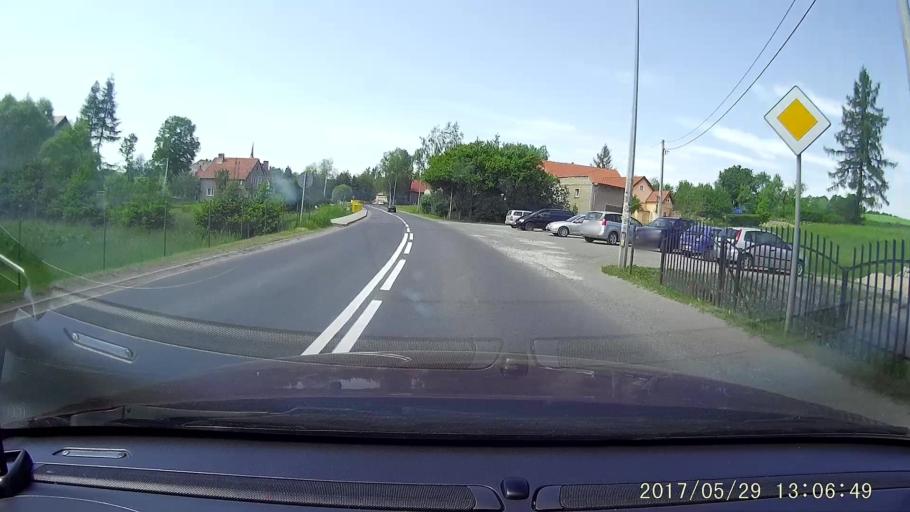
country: PL
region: Lower Silesian Voivodeship
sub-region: Powiat jeleniogorski
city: Stara Kamienica
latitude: 50.9538
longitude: 15.5792
